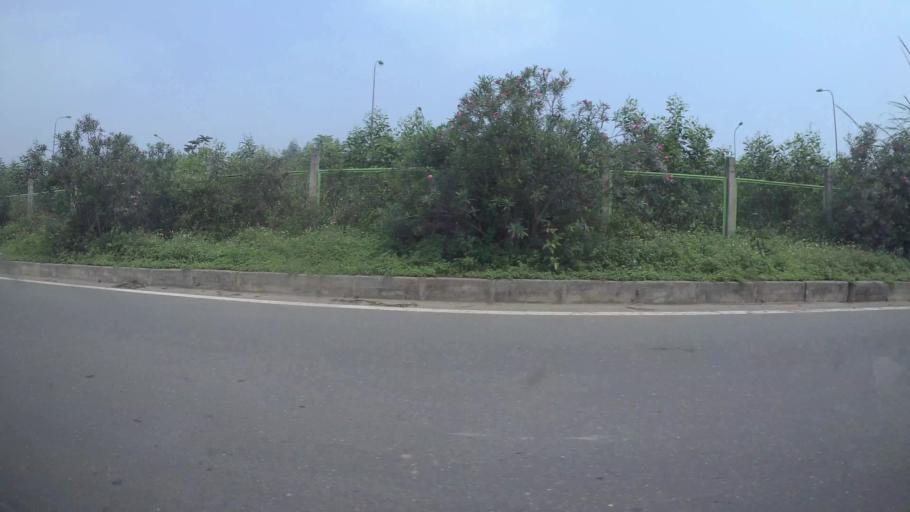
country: VN
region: Ha Noi
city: Quoc Oai
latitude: 20.9938
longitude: 105.5879
